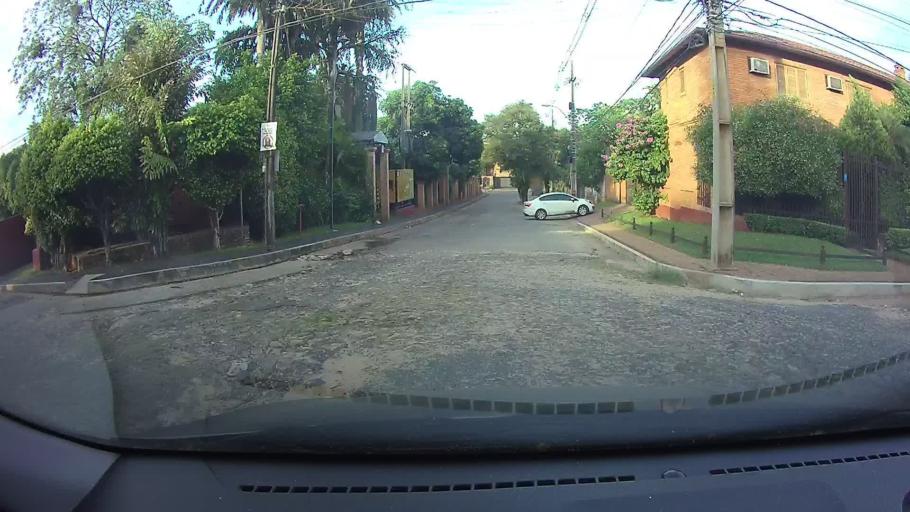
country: PY
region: Asuncion
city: Asuncion
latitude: -25.2748
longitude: -57.5699
